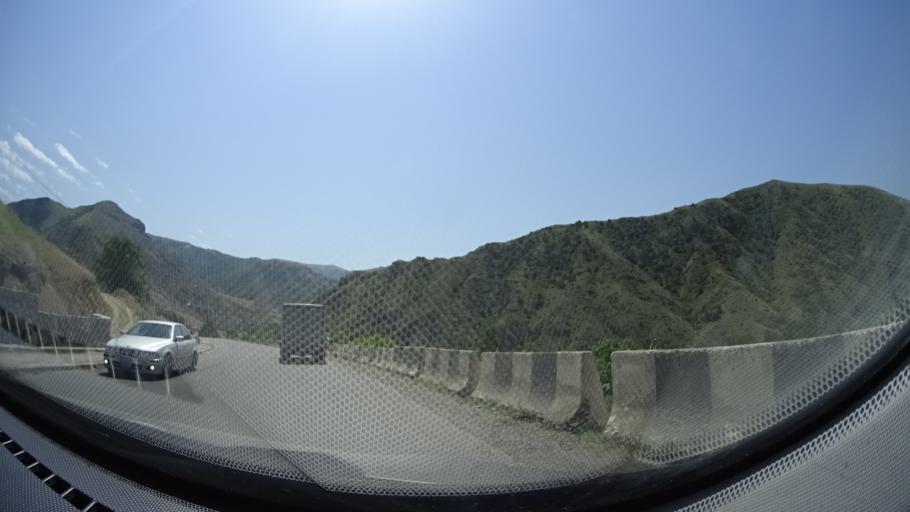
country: GE
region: Samtskhe-Javakheti
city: Aspindza
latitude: 41.5656
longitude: 43.2587
